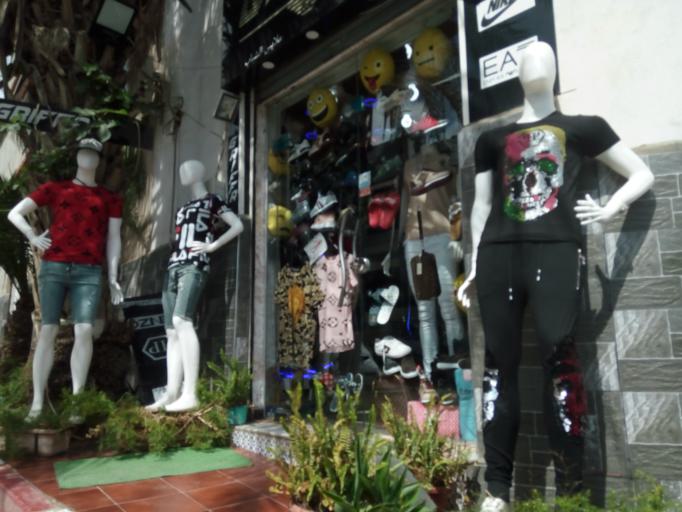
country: DZ
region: Tipaza
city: Douera
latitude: 36.6989
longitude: 2.9709
